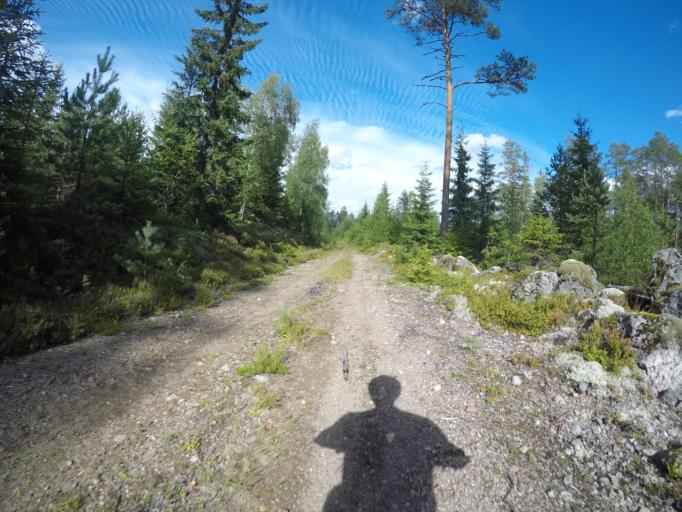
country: SE
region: OErebro
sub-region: Hallefors Kommun
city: Haellefors
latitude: 60.0143
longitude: 14.5957
